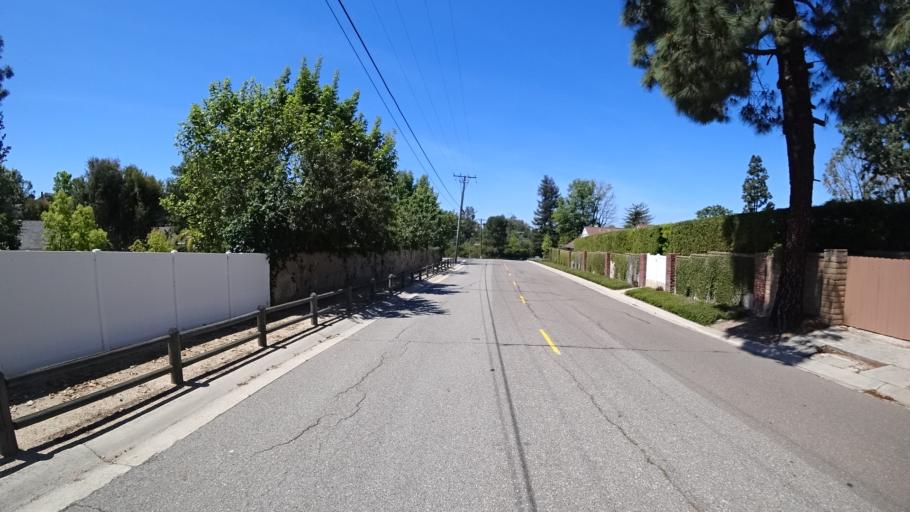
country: US
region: California
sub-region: Orange County
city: Villa Park
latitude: 33.8254
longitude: -117.7980
